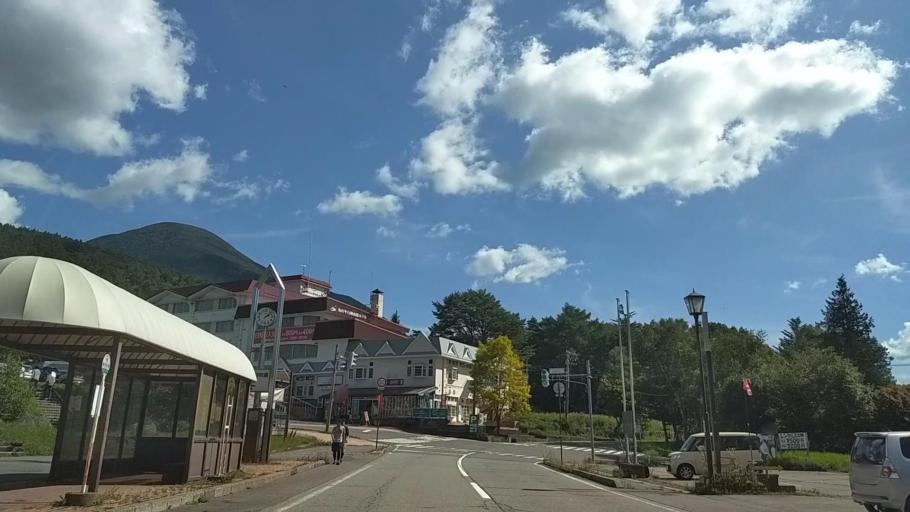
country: JP
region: Nagano
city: Chino
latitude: 36.1296
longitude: 138.2717
